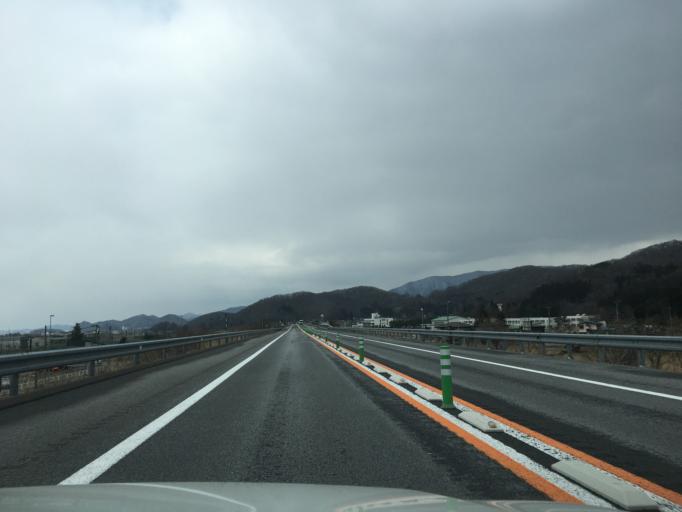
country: JP
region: Aomori
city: Aomori Shi
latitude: 40.8067
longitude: 140.7978
